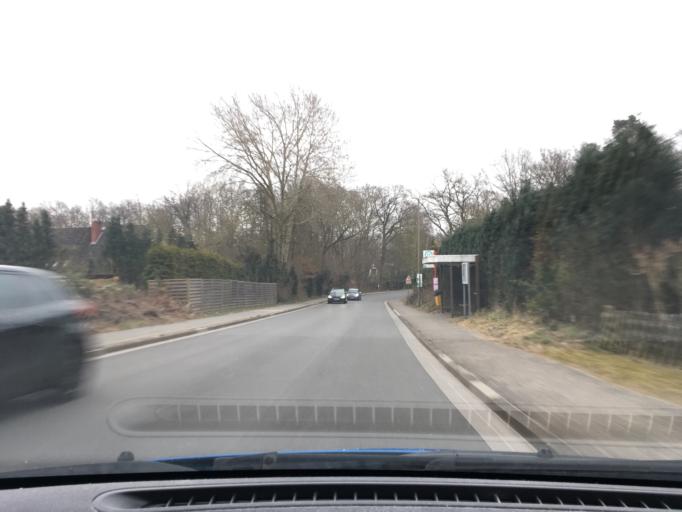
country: DE
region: Lower Saxony
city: Vogelsen
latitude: 53.2735
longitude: 10.3583
